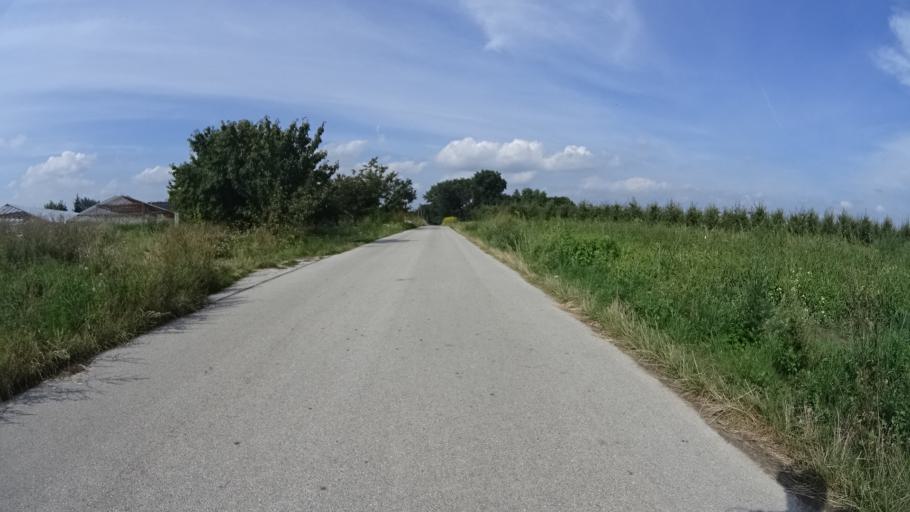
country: PL
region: Masovian Voivodeship
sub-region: Powiat grojecki
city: Goszczyn
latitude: 51.6962
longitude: 20.8476
